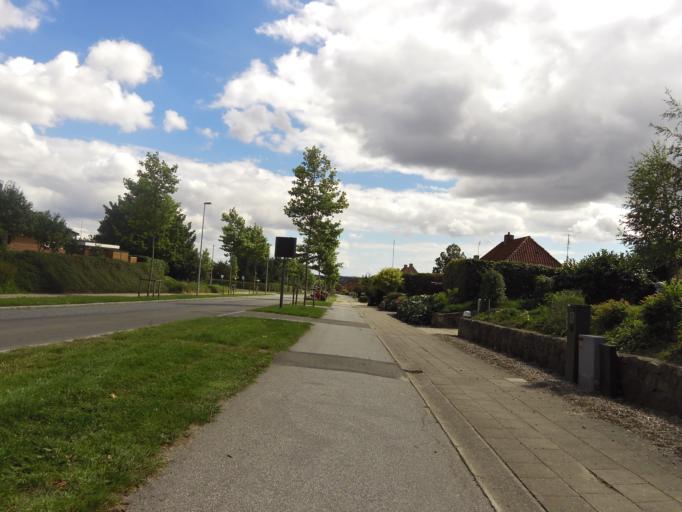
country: DK
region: South Denmark
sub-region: Haderslev Kommune
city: Haderslev
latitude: 55.2526
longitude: 9.4578
